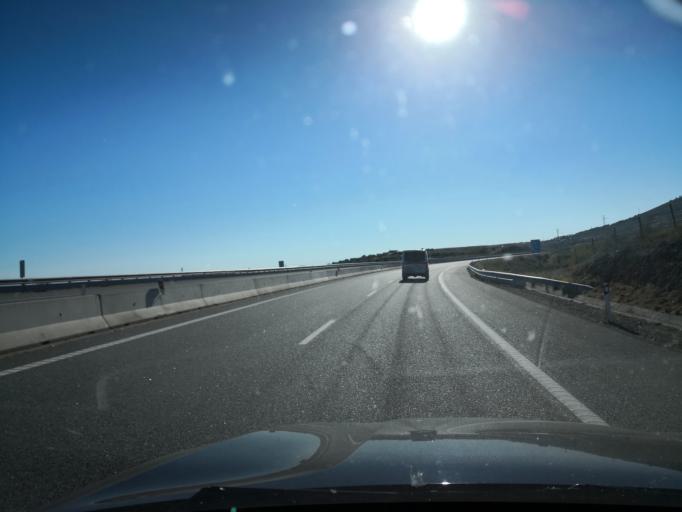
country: PT
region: Braganca
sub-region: Mirandela
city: Mirandela
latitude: 41.4519
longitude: -7.2668
